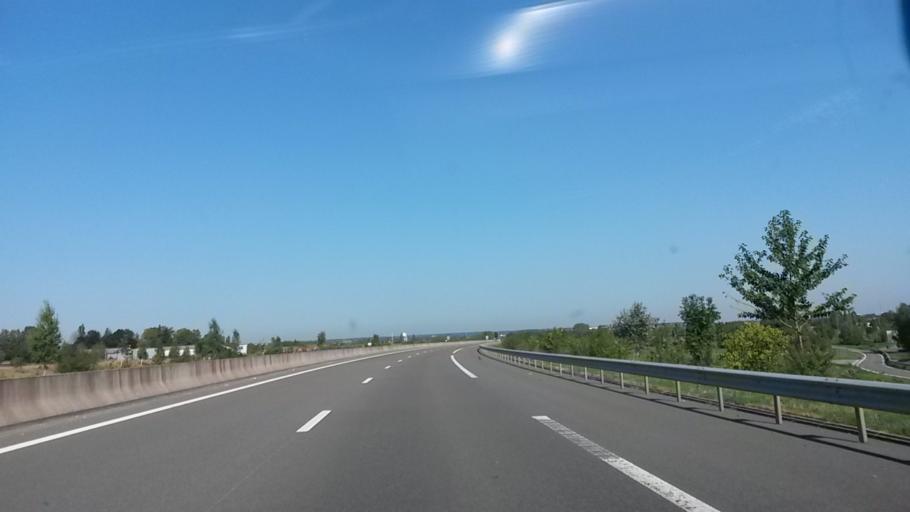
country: FR
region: Nord-Pas-de-Calais
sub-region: Departement du Nord
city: Louvroil
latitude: 50.2437
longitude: 3.9546
